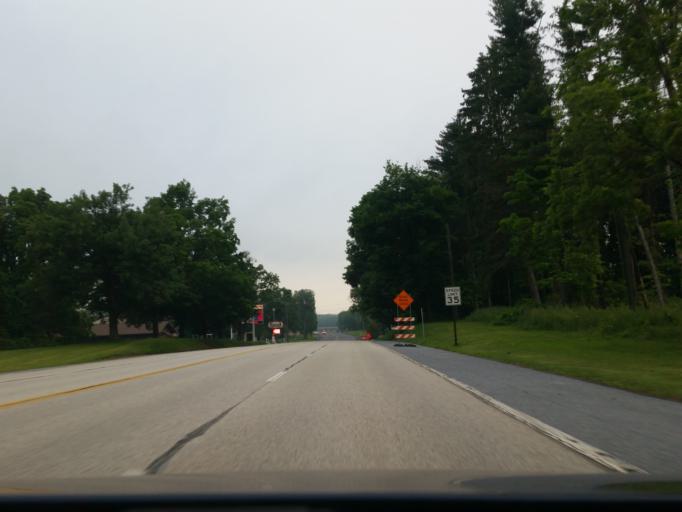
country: US
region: Pennsylvania
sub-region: Lebanon County
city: Jonestown
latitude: 40.4230
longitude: -76.5760
